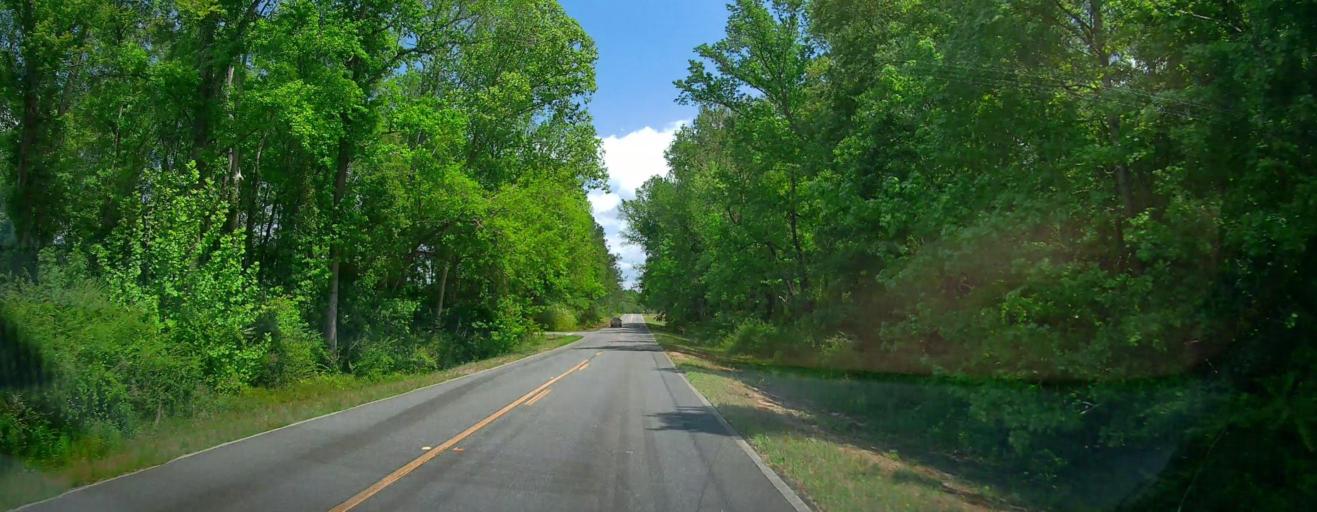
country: US
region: Georgia
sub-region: Treutlen County
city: Soperton
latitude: 32.5161
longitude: -82.6577
